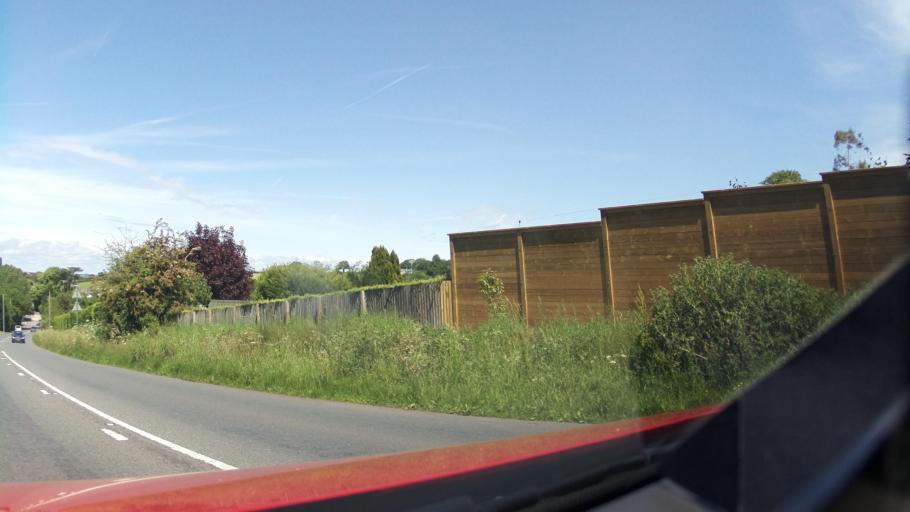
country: GB
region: England
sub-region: Devon
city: Topsham
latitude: 50.6794
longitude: -3.4443
